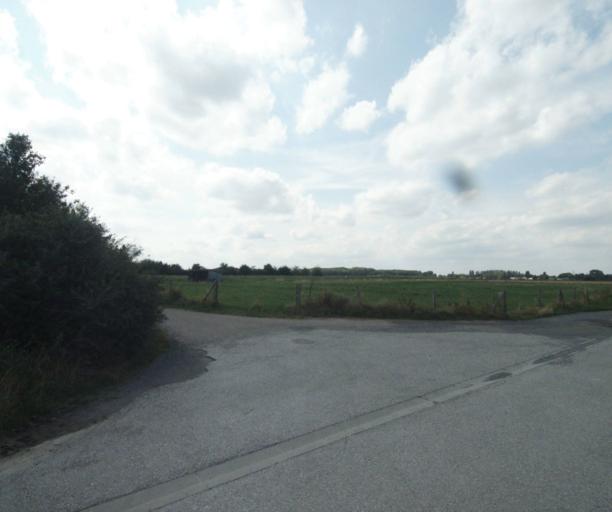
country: FR
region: Nord-Pas-de-Calais
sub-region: Departement du Nord
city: Forest-sur-Marque
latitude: 50.6405
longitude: 3.1796
